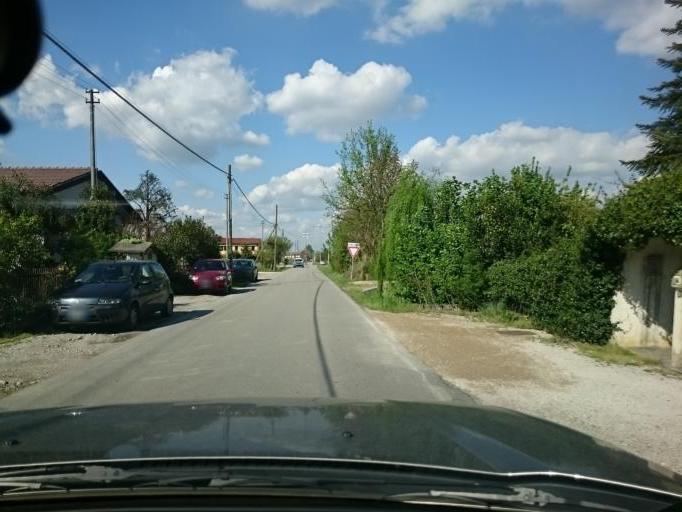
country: IT
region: Veneto
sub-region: Provincia di Venezia
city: Caselle
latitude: 45.5047
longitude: 11.9925
